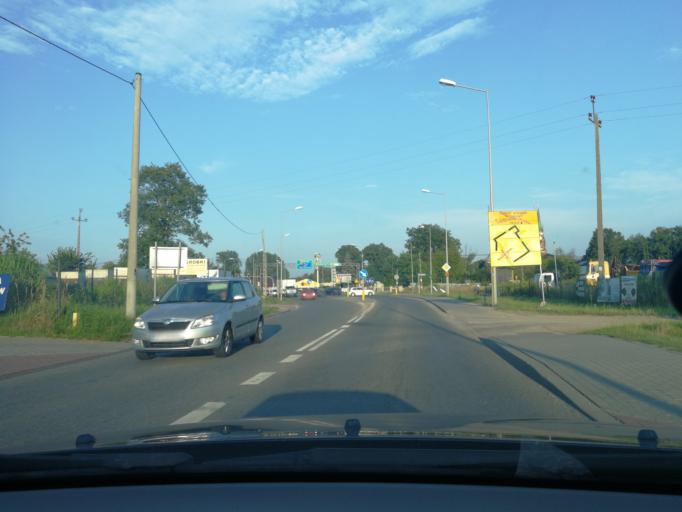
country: PL
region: Masovian Voivodeship
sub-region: Powiat warszawski zachodni
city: Ozarow Mazowiecki
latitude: 52.1829
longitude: 20.7797
